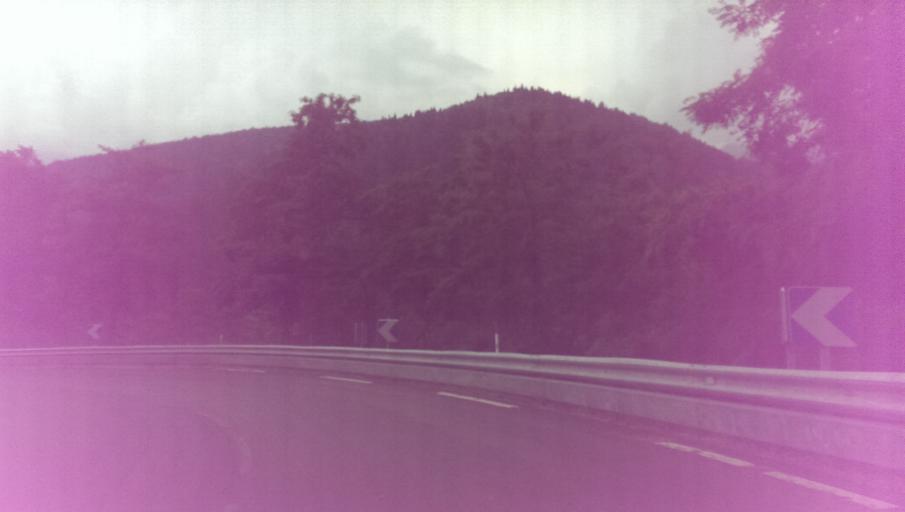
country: ES
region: Catalonia
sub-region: Provincia de Girona
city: Llivia
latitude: 42.5062
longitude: 2.1512
